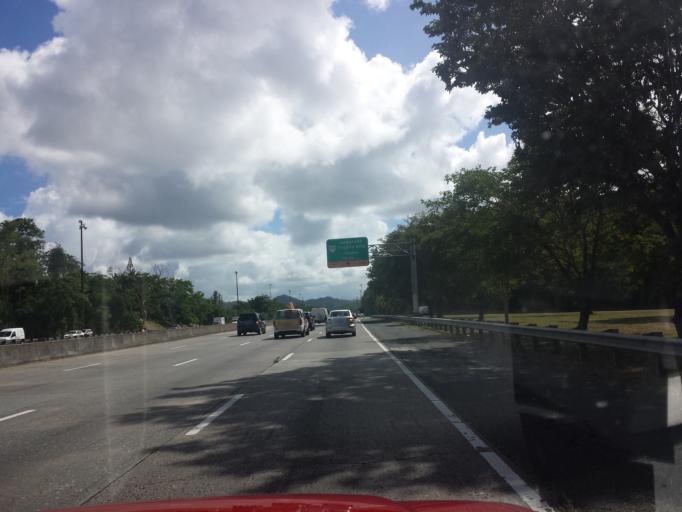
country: PR
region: Guaynabo
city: Guaynabo
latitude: 18.3691
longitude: -66.0703
